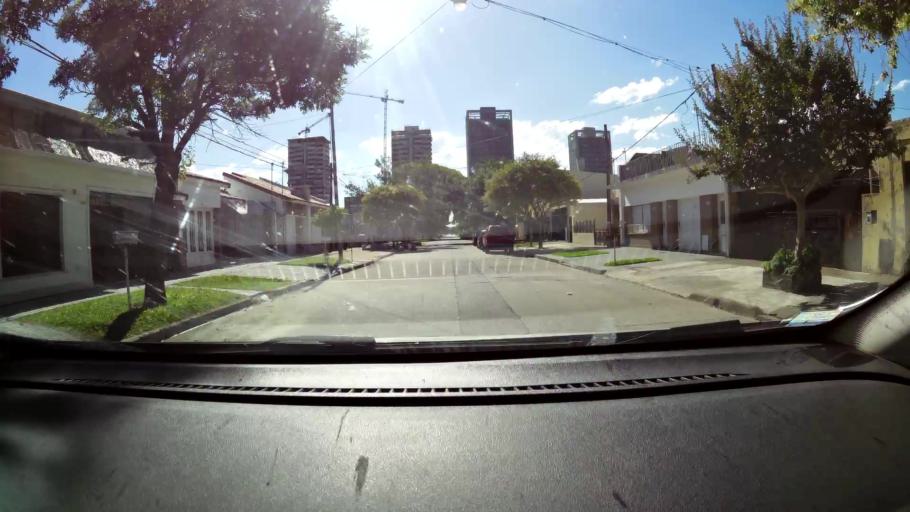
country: AR
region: Santa Fe
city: Santa Fe de la Vera Cruz
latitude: -31.6243
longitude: -60.6921
